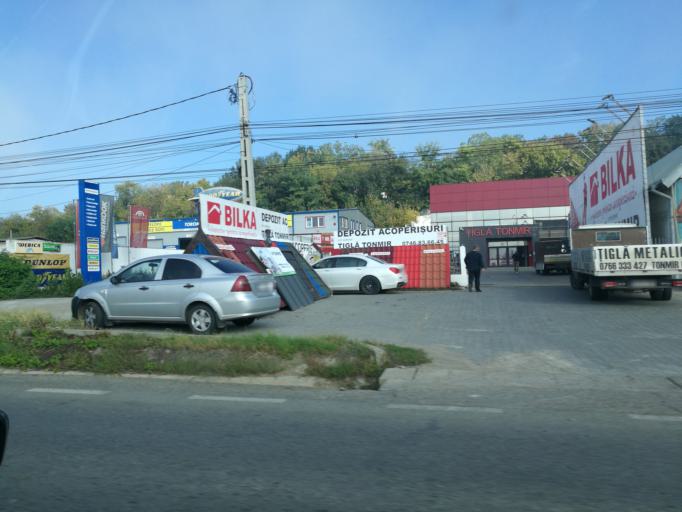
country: RO
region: Iasi
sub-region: Comuna Valea Lupului
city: Valea Lupului
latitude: 47.1726
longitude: 27.5214
